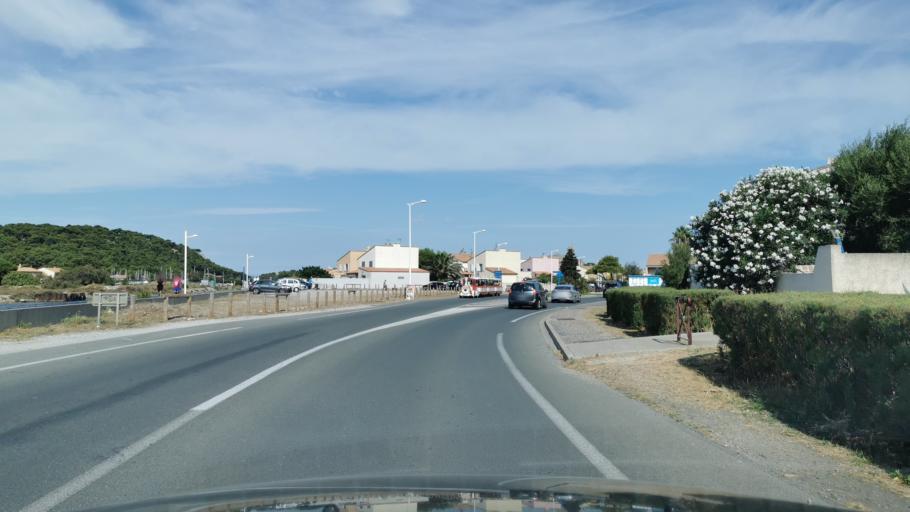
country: FR
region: Languedoc-Roussillon
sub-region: Departement de l'Aude
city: Gruissan
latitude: 43.1026
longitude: 3.0912
